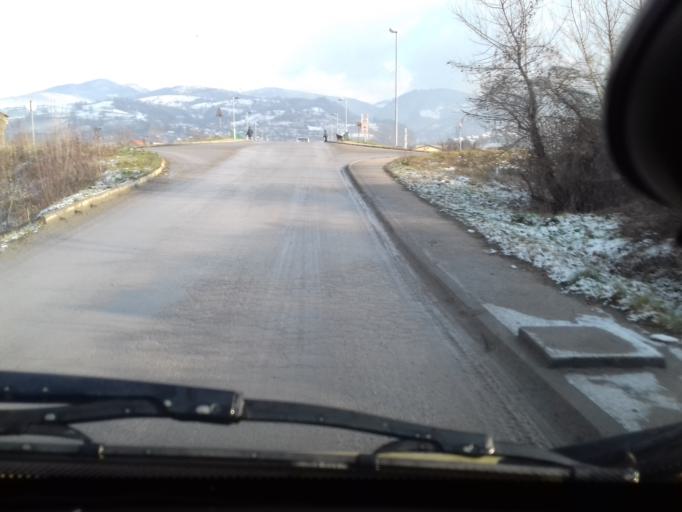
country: BA
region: Federation of Bosnia and Herzegovina
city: Zenica
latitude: 44.2175
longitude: 17.9100
